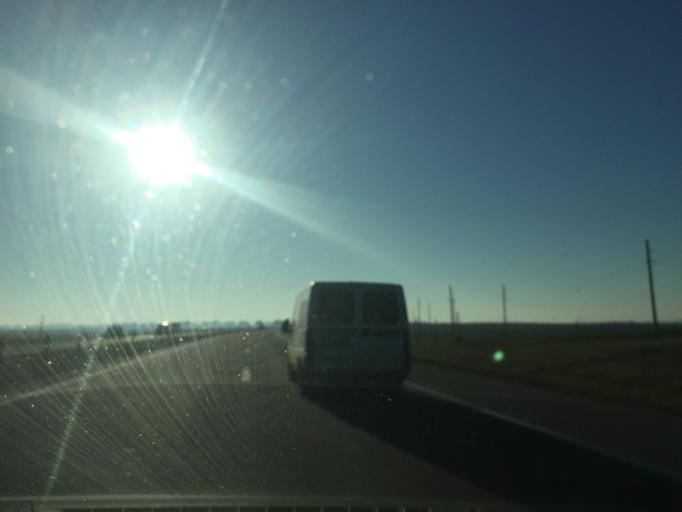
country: BY
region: Minsk
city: Luhavaya Slabada
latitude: 53.7739
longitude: 27.8565
